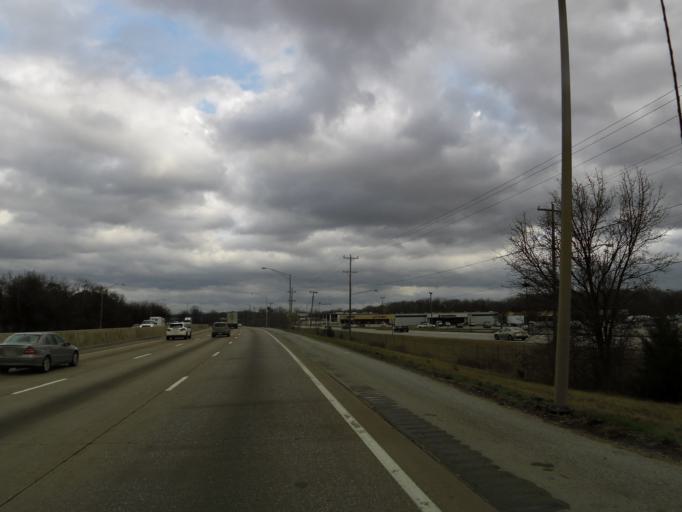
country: US
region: Tennessee
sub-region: Hamilton County
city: East Ridge
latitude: 35.0046
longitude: -85.2255
